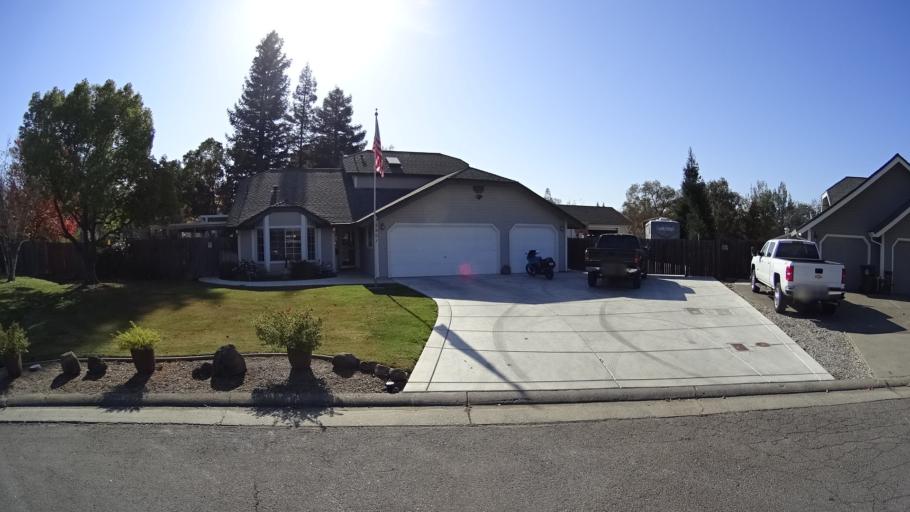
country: US
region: California
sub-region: Sacramento County
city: Citrus Heights
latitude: 38.6916
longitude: -121.2803
